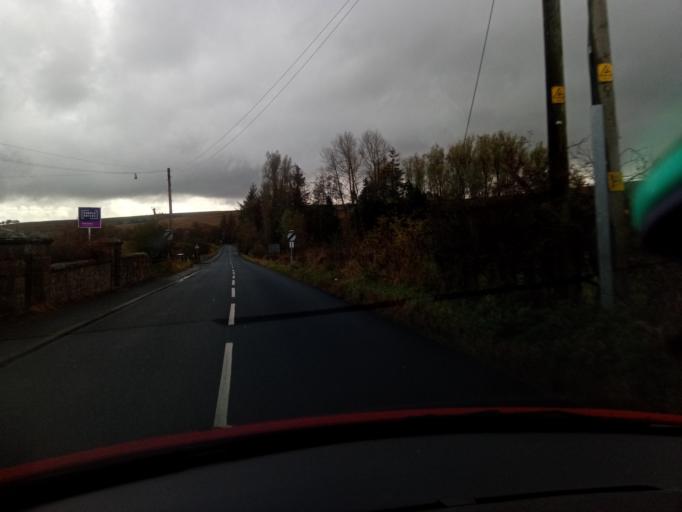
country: GB
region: England
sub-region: Northumberland
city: Birtley
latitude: 55.1399
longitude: -2.2613
